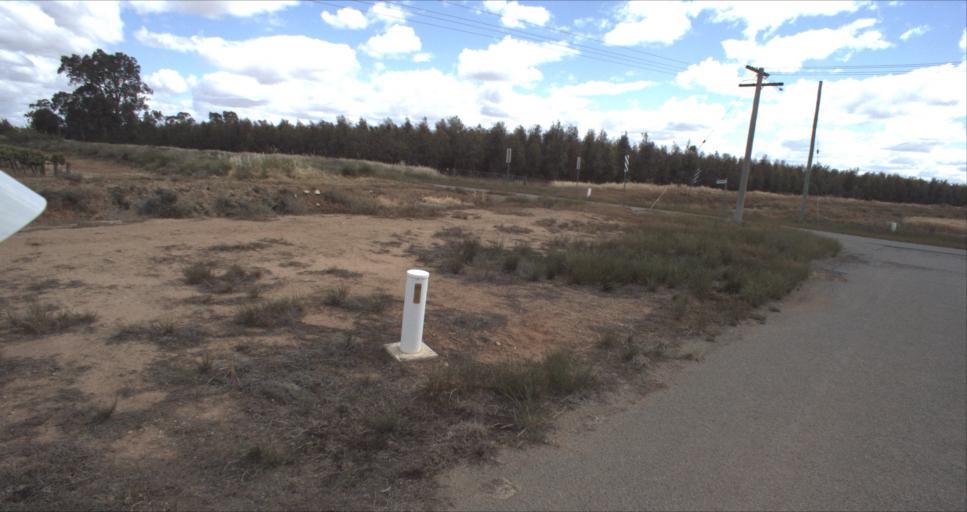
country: AU
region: New South Wales
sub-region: Leeton
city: Leeton
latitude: -34.5740
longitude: 146.3987
